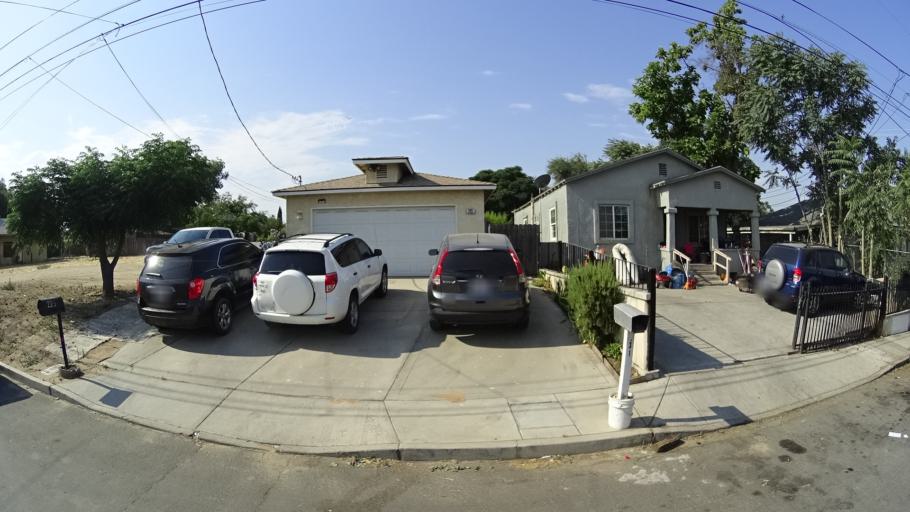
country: US
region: California
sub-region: Fresno County
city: West Park
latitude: 36.7205
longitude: -119.8152
